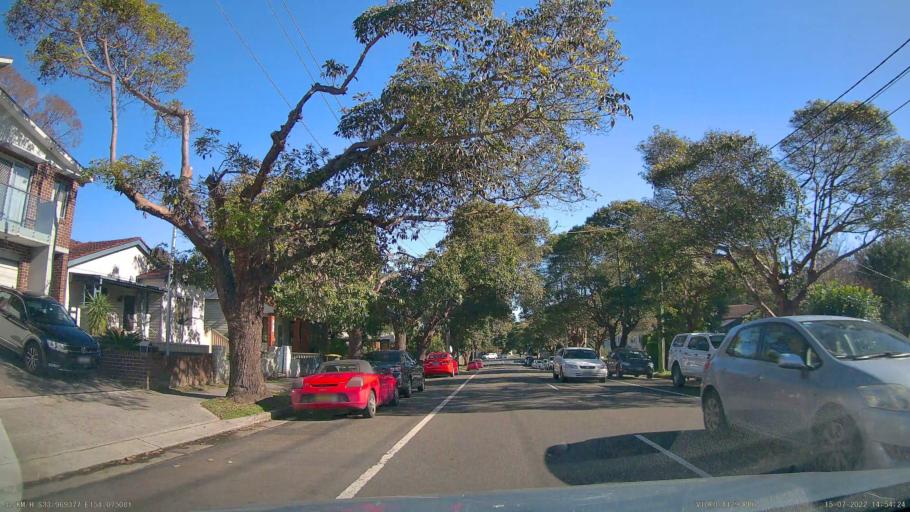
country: AU
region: New South Wales
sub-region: Hurstville
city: Penshurst
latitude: -33.9694
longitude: 151.0750
